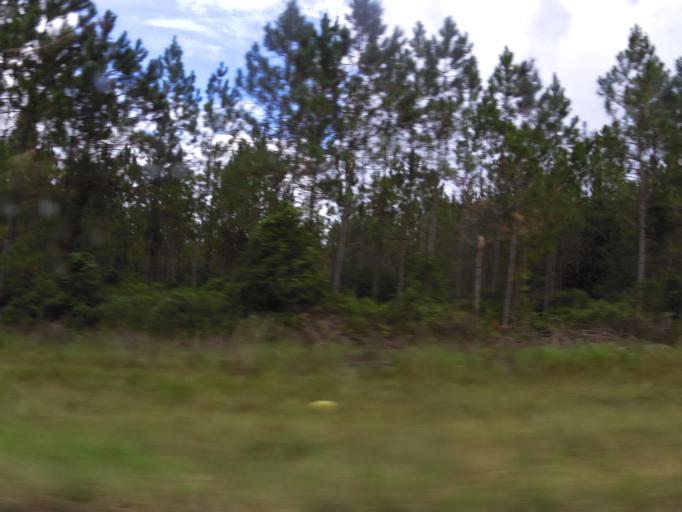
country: US
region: Florida
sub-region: Nassau County
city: Hilliard
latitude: 30.5914
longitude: -82.0480
